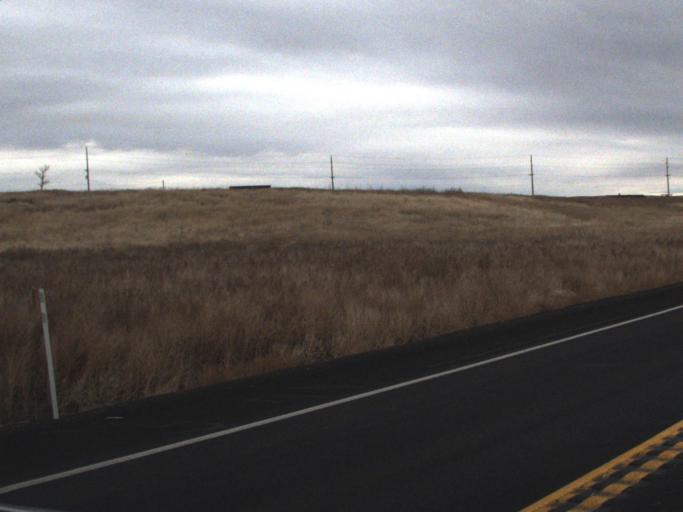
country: US
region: Washington
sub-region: Walla Walla County
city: Garrett
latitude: 46.0403
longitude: -118.6546
